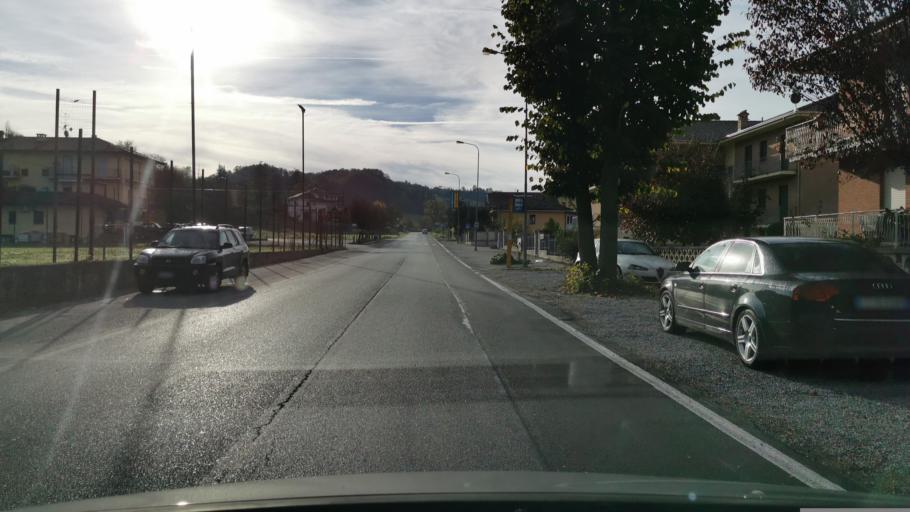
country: IT
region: Piedmont
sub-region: Provincia di Cuneo
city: Monchiero Borgonuovo
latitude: 44.5667
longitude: 7.9195
